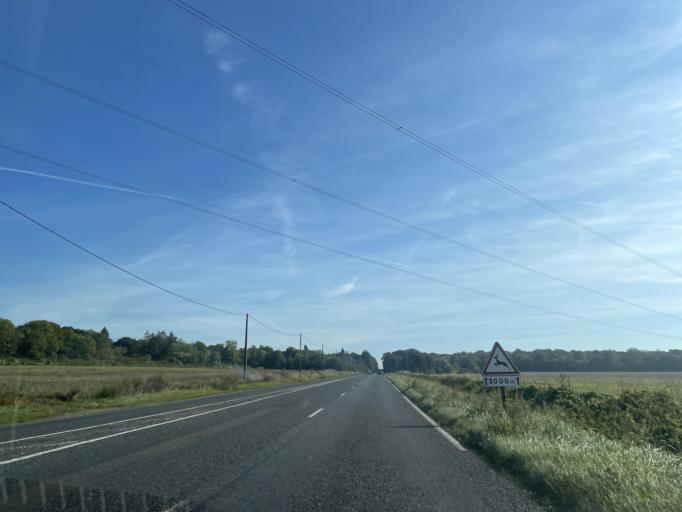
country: FR
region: Ile-de-France
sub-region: Departement de Seine-et-Marne
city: Trilport
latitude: 48.9582
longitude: 2.9647
